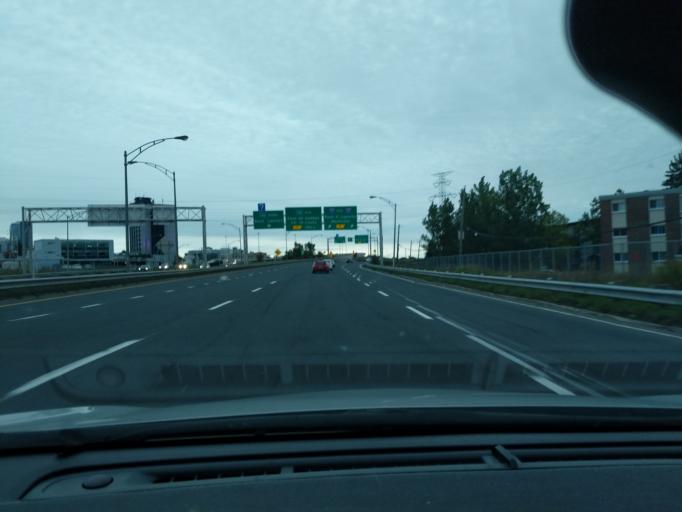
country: CA
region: Quebec
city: L'Ancienne-Lorette
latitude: 46.7616
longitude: -71.3049
